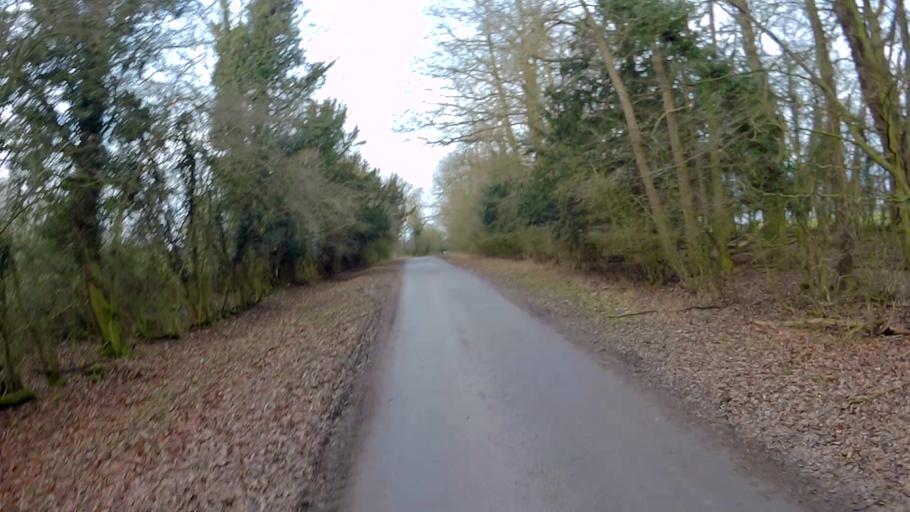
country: GB
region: England
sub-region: Lincolnshire
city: Bourne
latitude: 52.8191
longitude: -0.4380
